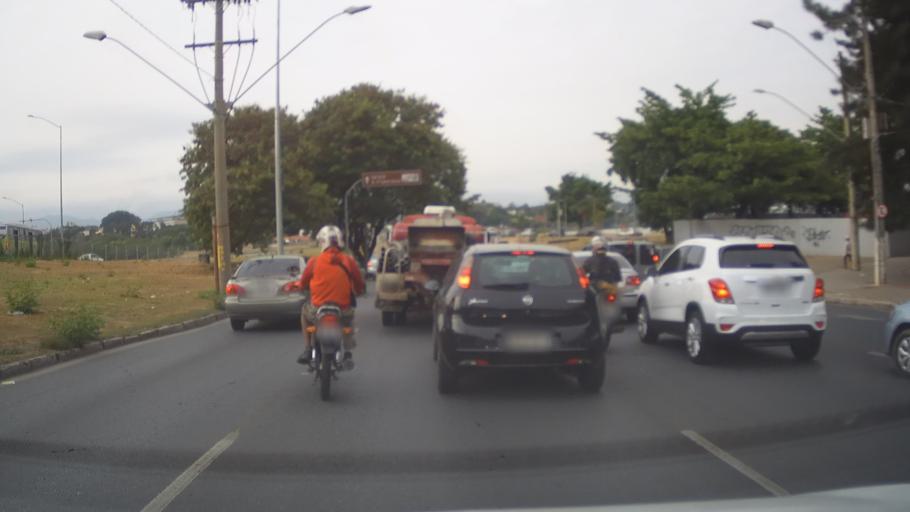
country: BR
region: Minas Gerais
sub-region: Belo Horizonte
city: Belo Horizonte
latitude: -19.8433
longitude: -43.9673
